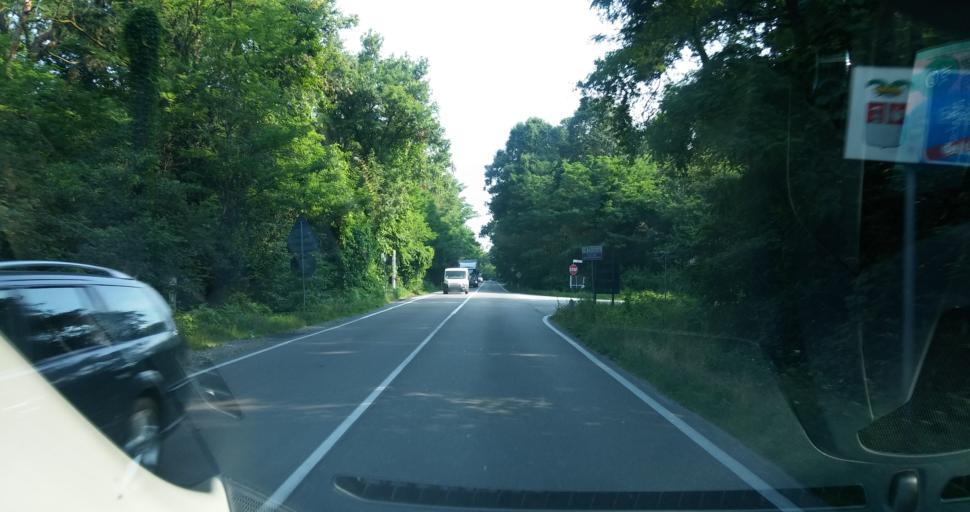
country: IT
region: Lombardy
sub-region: Provincia di Varese
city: Vizzola Ticino
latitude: 45.6468
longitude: 8.7040
